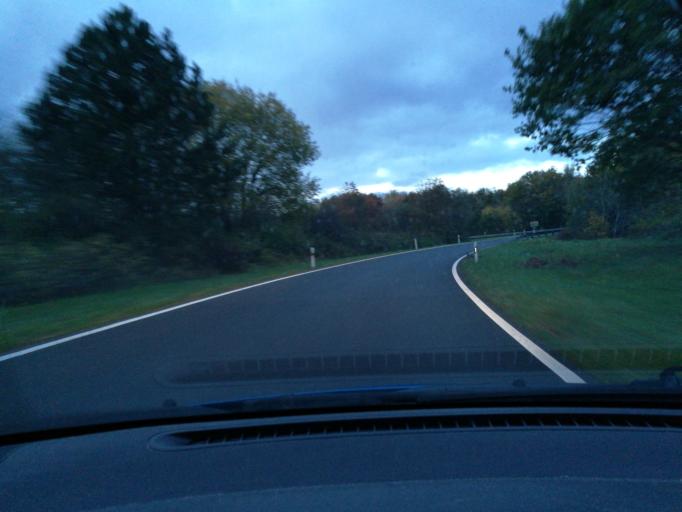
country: DE
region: Schleswig-Holstein
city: Busdorf
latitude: 54.4807
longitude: 9.5374
